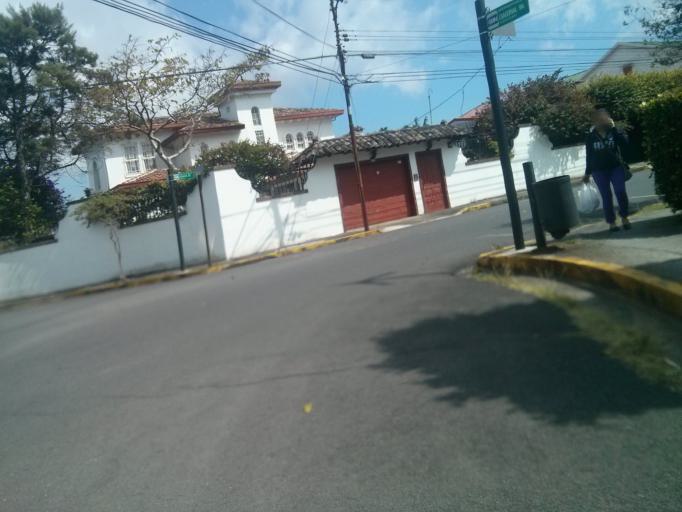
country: CR
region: San Jose
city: Calle Blancos
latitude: 9.9373
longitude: -84.0643
